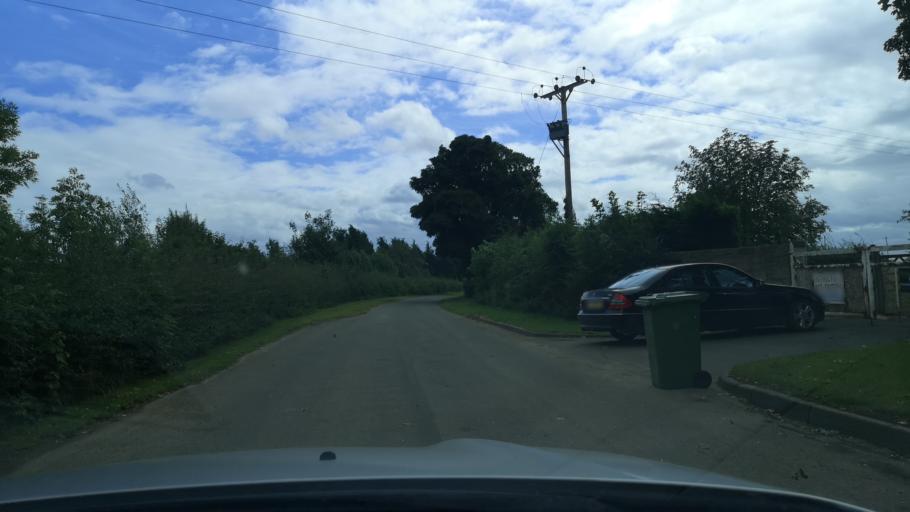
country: GB
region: England
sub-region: City and Borough of Wakefield
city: Darrington
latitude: 53.6796
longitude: -1.2607
